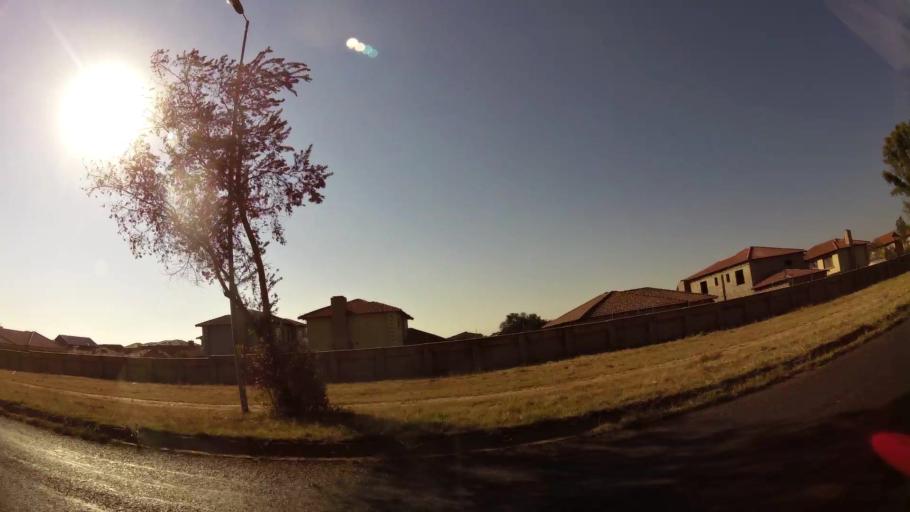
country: ZA
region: Gauteng
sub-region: City of Tshwane Metropolitan Municipality
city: Pretoria
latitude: -25.6637
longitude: 28.1321
